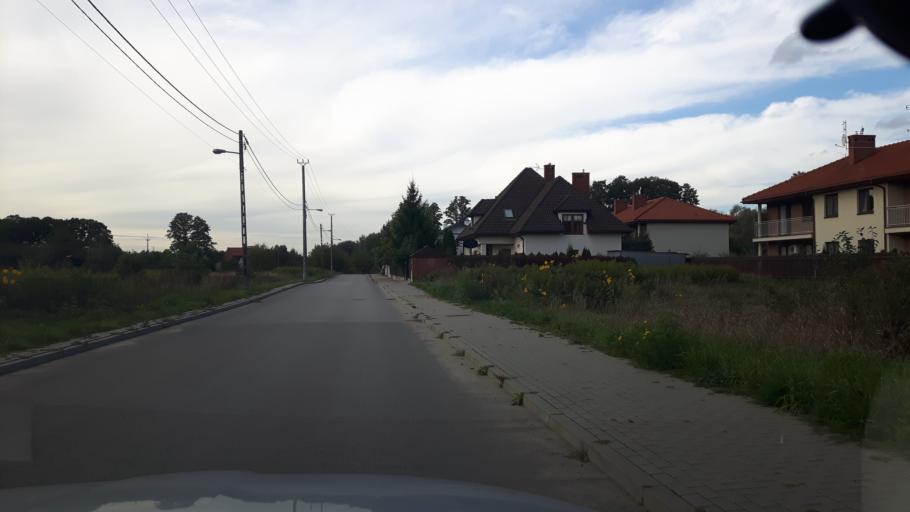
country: PL
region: Masovian Voivodeship
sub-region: Powiat legionowski
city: Stanislawow Pierwszy
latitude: 52.3473
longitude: 21.0500
